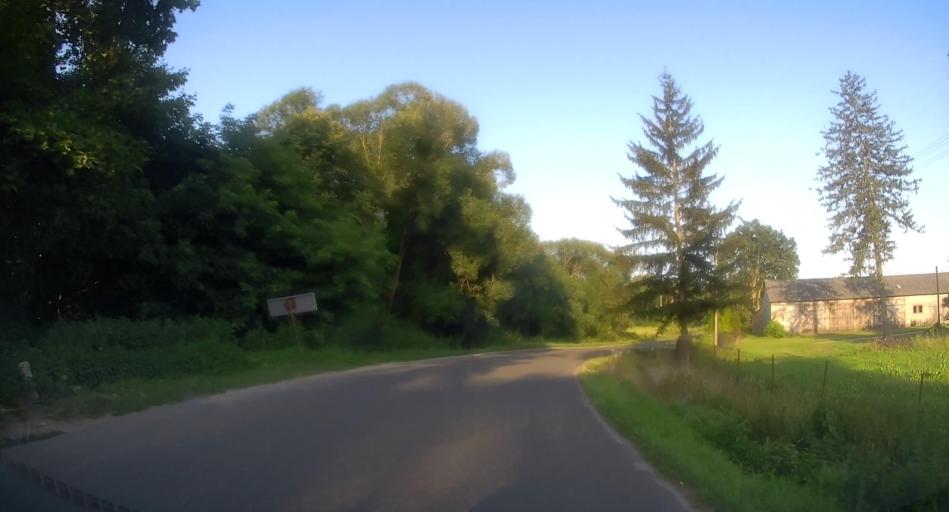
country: PL
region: Lodz Voivodeship
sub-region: Powiat skierniewicki
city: Kaweczyn Nowy
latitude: 51.9001
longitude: 20.3009
